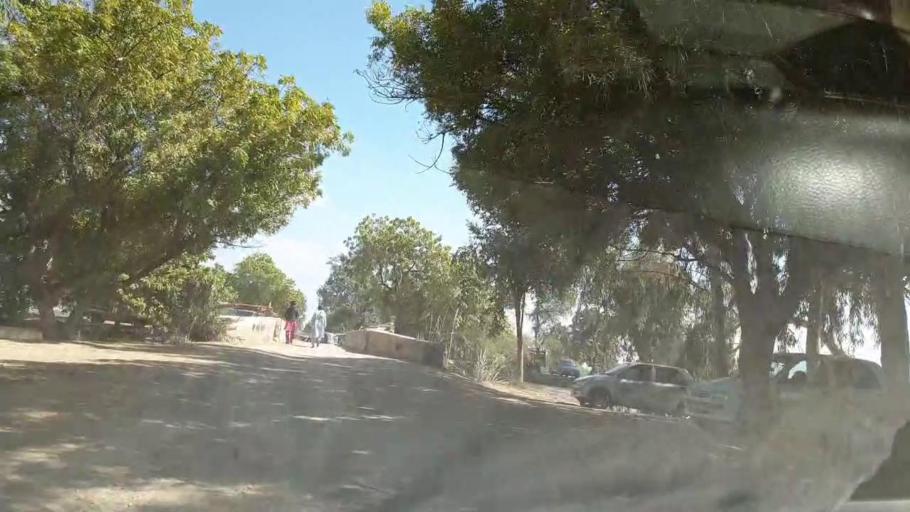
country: PK
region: Sindh
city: Pithoro
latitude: 25.6071
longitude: 69.2143
